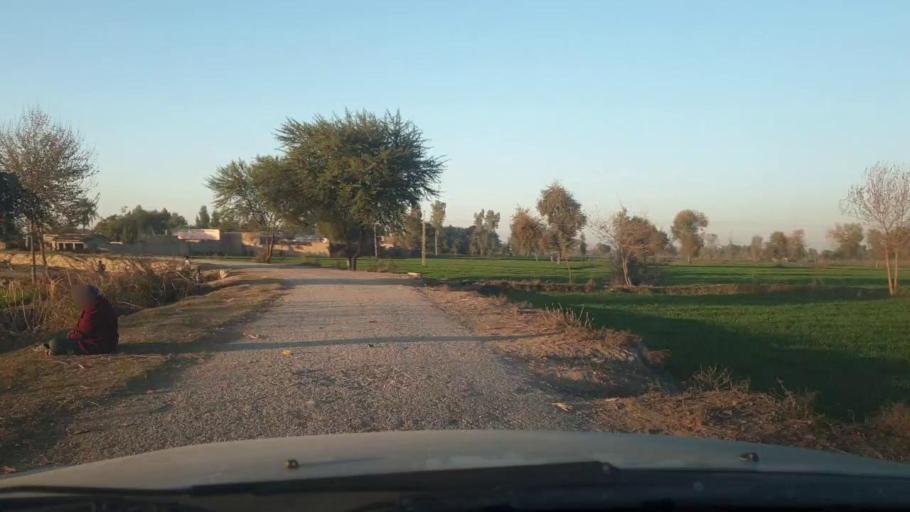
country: PK
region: Sindh
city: Pano Aqil
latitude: 27.9116
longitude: 69.1983
